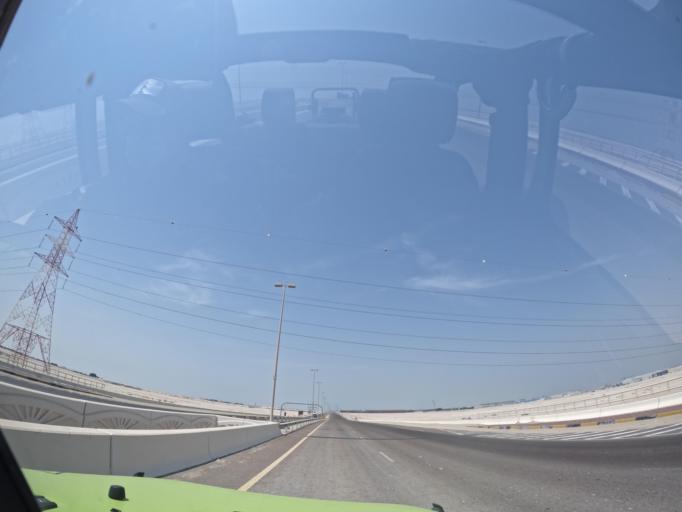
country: AE
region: Abu Dhabi
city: Abu Dhabi
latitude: 24.2555
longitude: 54.4641
